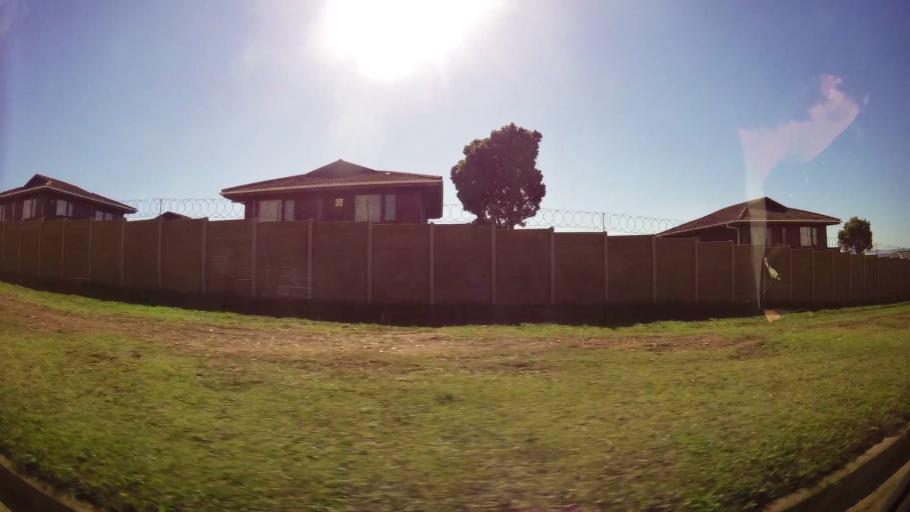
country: ZA
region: Eastern Cape
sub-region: Cacadu District Municipality
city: Jeffrey's Bay
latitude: -34.0544
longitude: 24.9160
